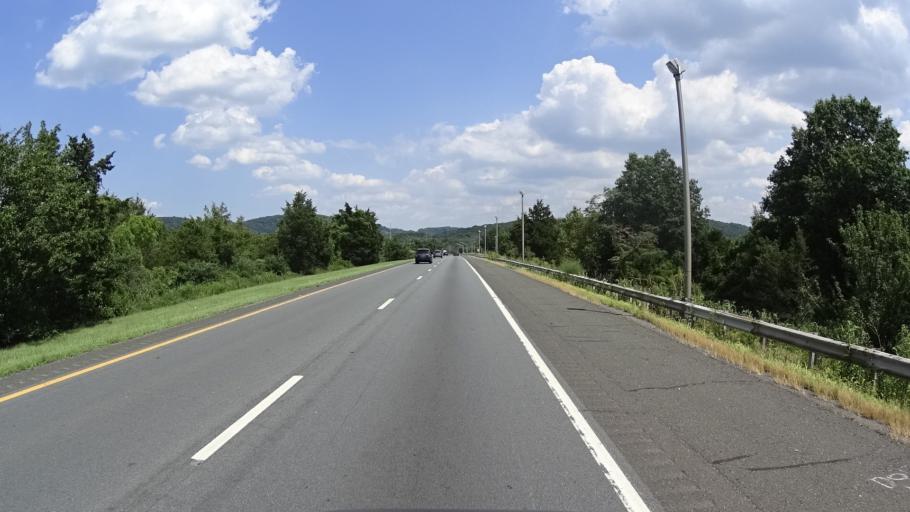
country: US
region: New Jersey
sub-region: Somerset County
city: Bedminster
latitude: 40.6429
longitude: -74.6501
